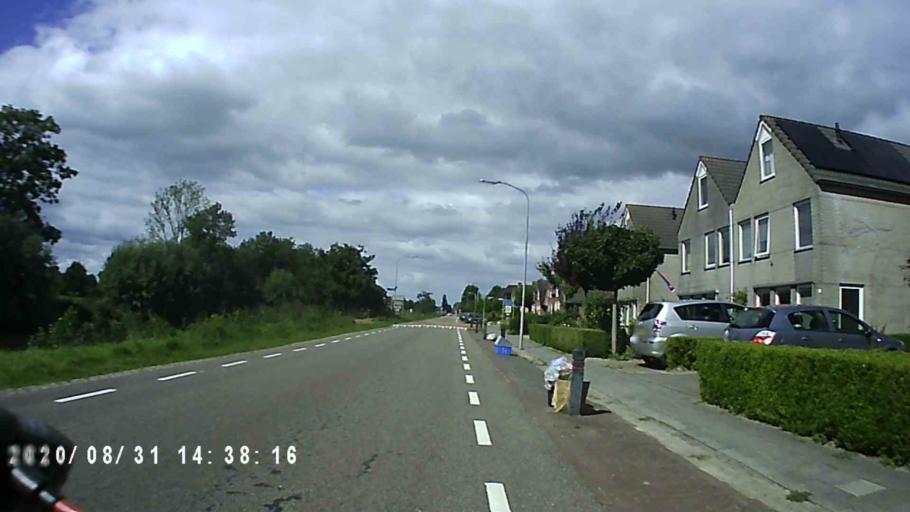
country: NL
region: Groningen
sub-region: Gemeente Zuidhorn
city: Zuidhorn
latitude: 53.2396
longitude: 6.3914
